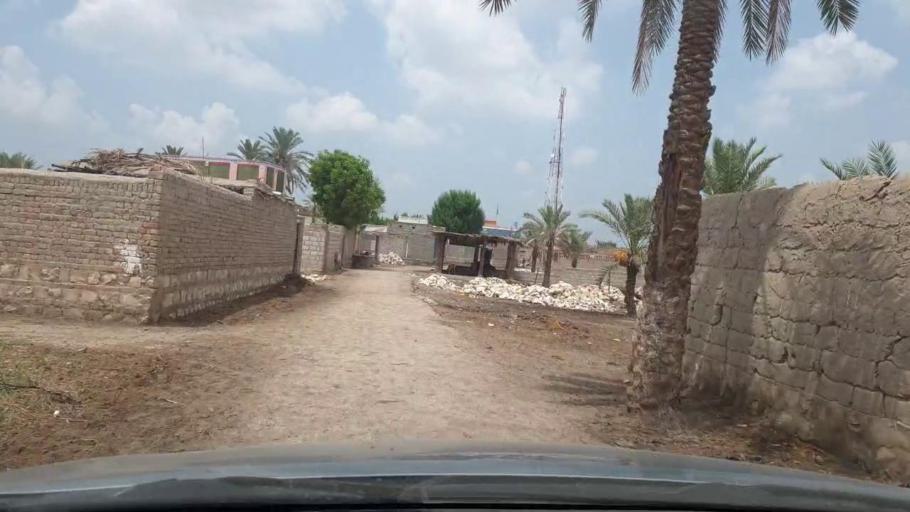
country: PK
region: Sindh
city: Khairpur
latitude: 27.4283
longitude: 68.7711
